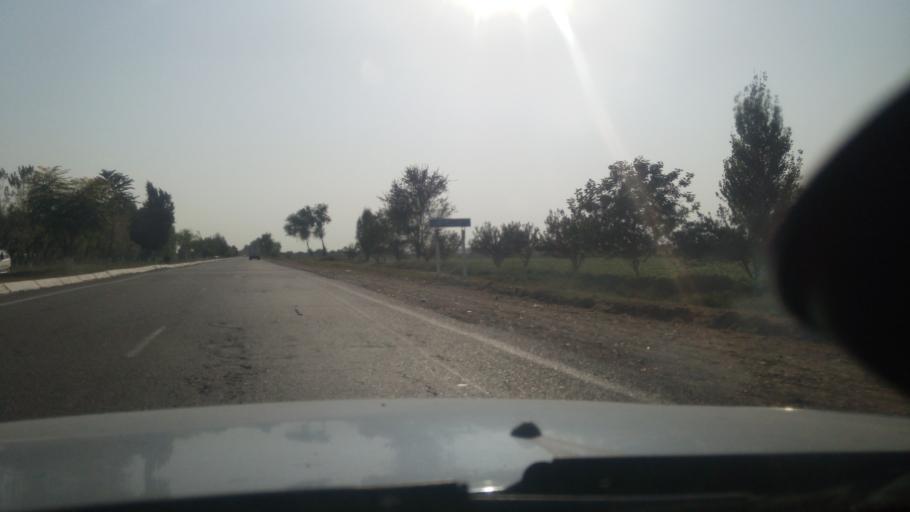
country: UZ
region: Toshkent
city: Zafar
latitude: 41.0072
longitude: 68.8324
